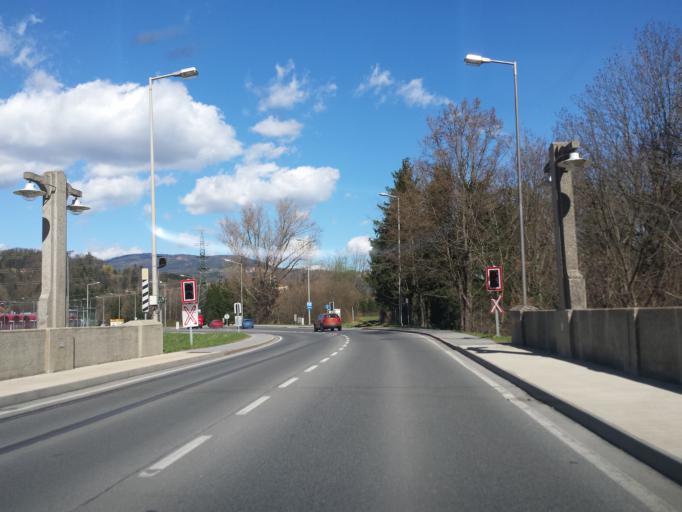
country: AT
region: Styria
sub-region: Graz Stadt
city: Goesting
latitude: 47.1067
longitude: 15.4017
